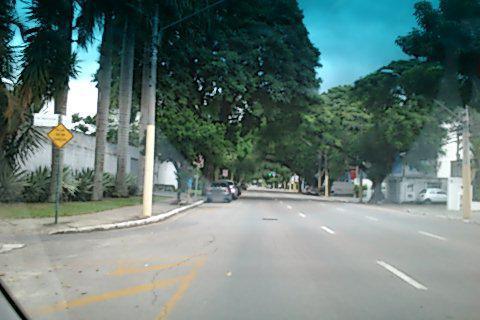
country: BR
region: Sao Paulo
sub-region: Sao Jose Dos Campos
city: Sao Jose dos Campos
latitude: -23.1988
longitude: -45.9000
